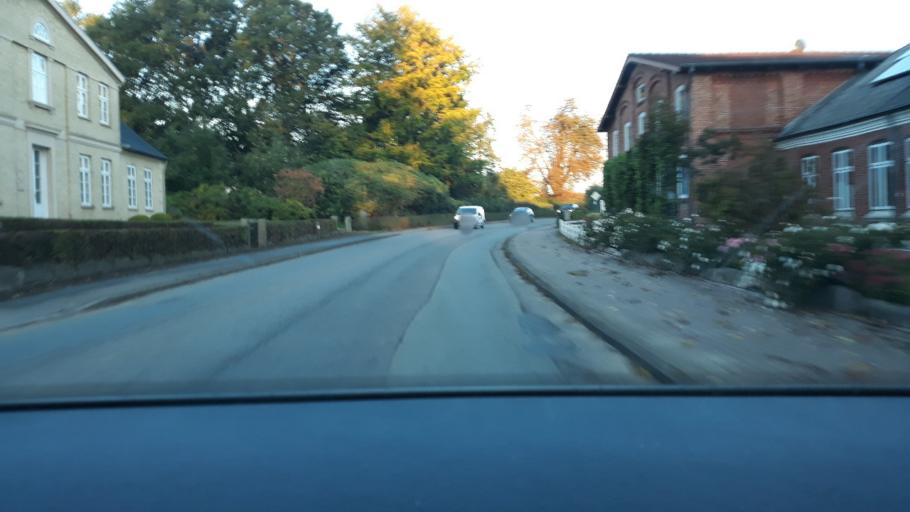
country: DE
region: Schleswig-Holstein
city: Ulsby
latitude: 54.6314
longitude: 9.5940
